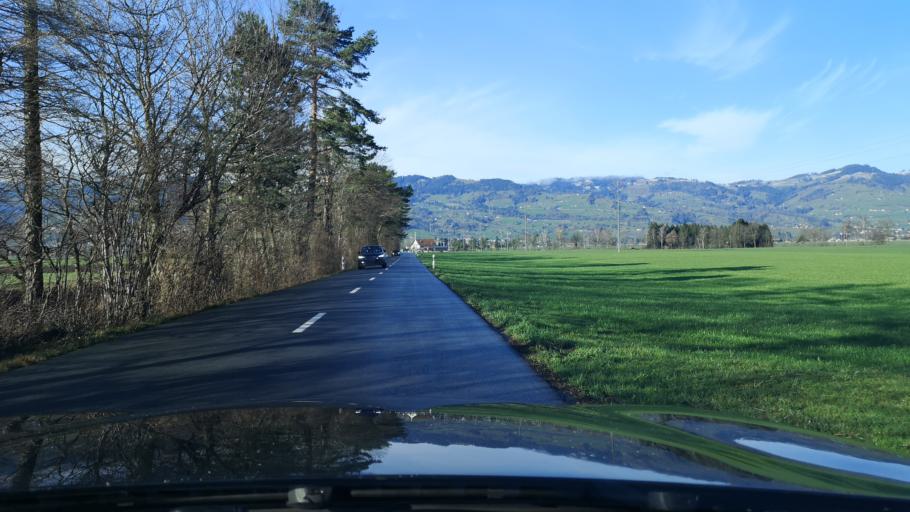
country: CH
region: Saint Gallen
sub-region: Wahlkreis Rheintal
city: Oberriet
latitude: 47.3415
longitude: 9.5708
